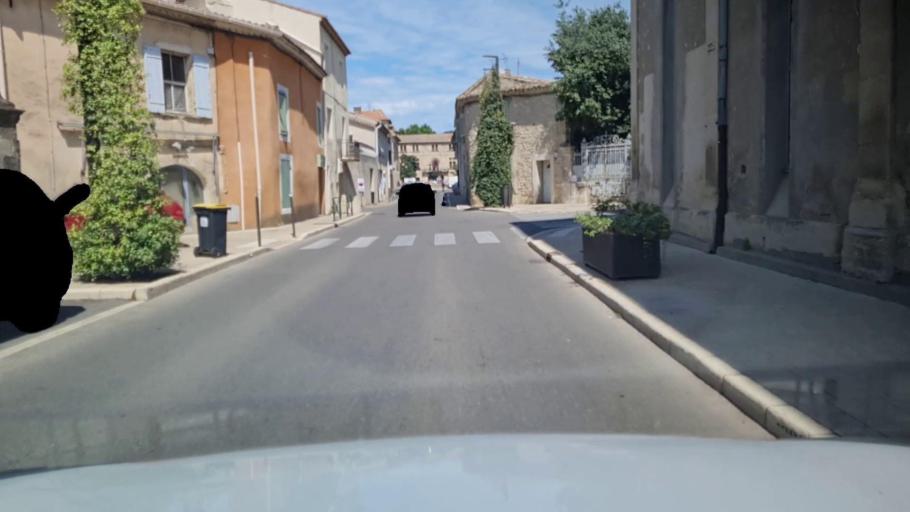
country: FR
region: Languedoc-Roussillon
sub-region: Departement du Gard
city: Caveirac
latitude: 43.8249
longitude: 4.2622
